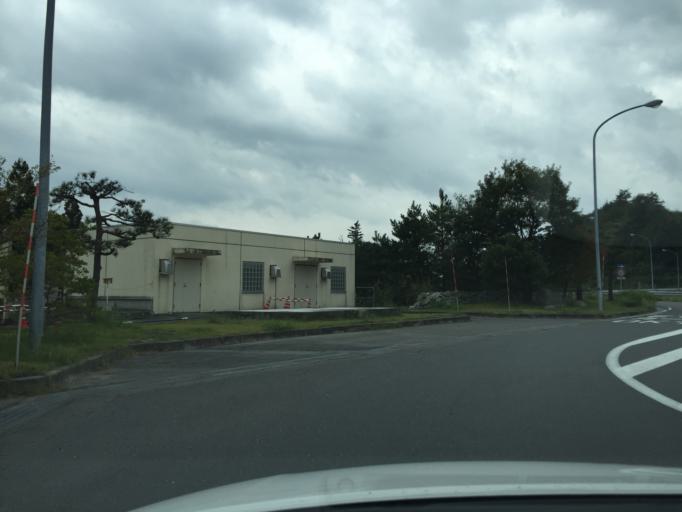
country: JP
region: Fukushima
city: Iwaki
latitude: 37.1756
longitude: 140.7218
